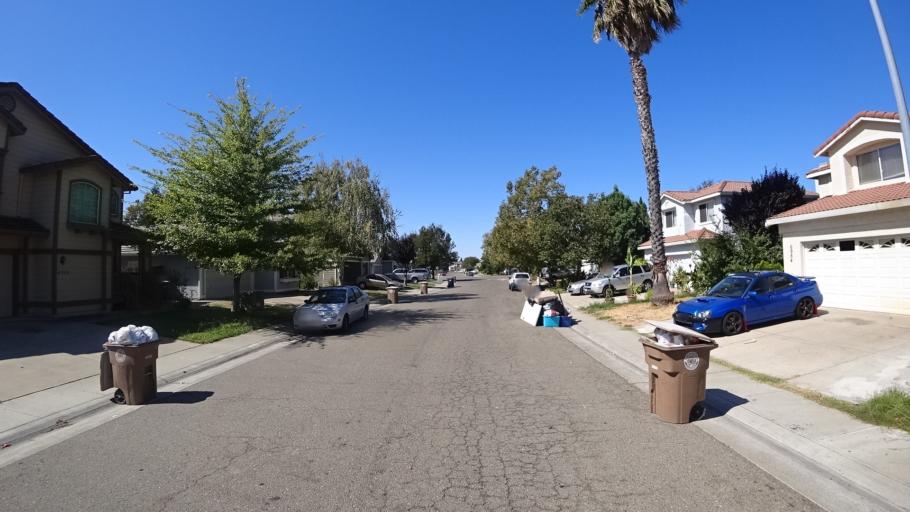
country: US
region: California
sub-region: Sacramento County
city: Laguna
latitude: 38.4240
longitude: -121.4237
